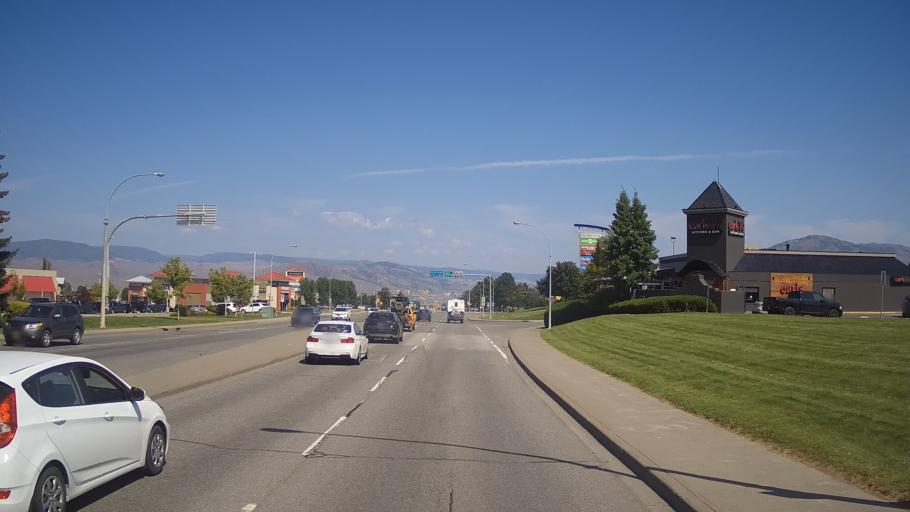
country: CA
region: British Columbia
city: Kamloops
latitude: 50.6644
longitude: -120.3538
